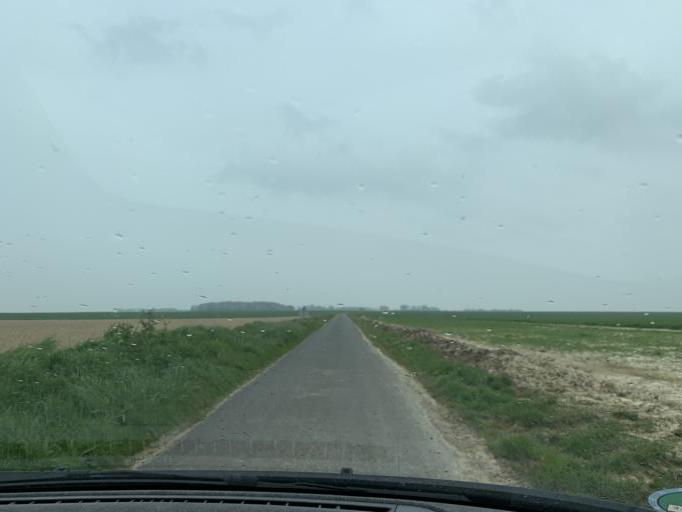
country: FR
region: Haute-Normandie
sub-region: Departement de la Seine-Maritime
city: Fontaine-le-Dun
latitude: 49.8574
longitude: 0.8239
